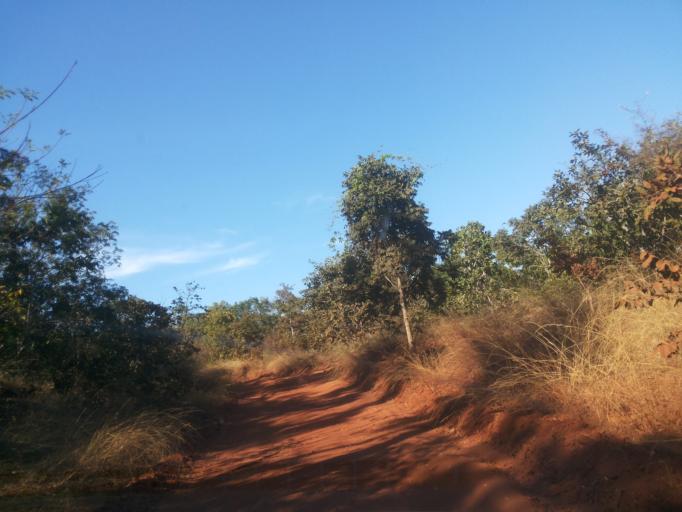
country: BR
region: Minas Gerais
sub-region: Ituiutaba
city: Ituiutaba
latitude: -19.0992
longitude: -49.4182
